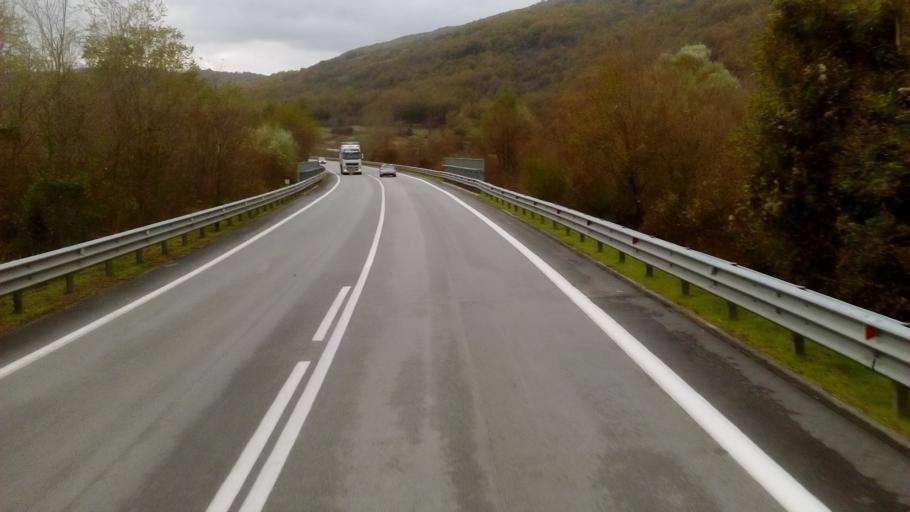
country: IT
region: Molise
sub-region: Provincia di Isernia
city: Sessano del Molise
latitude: 41.6341
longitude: 14.3164
